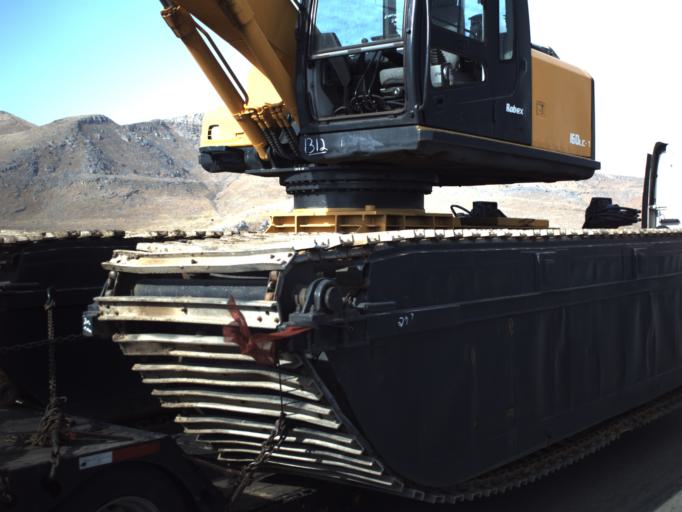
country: US
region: Utah
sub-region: Tooele County
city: Grantsville
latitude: 40.7341
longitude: -112.6012
